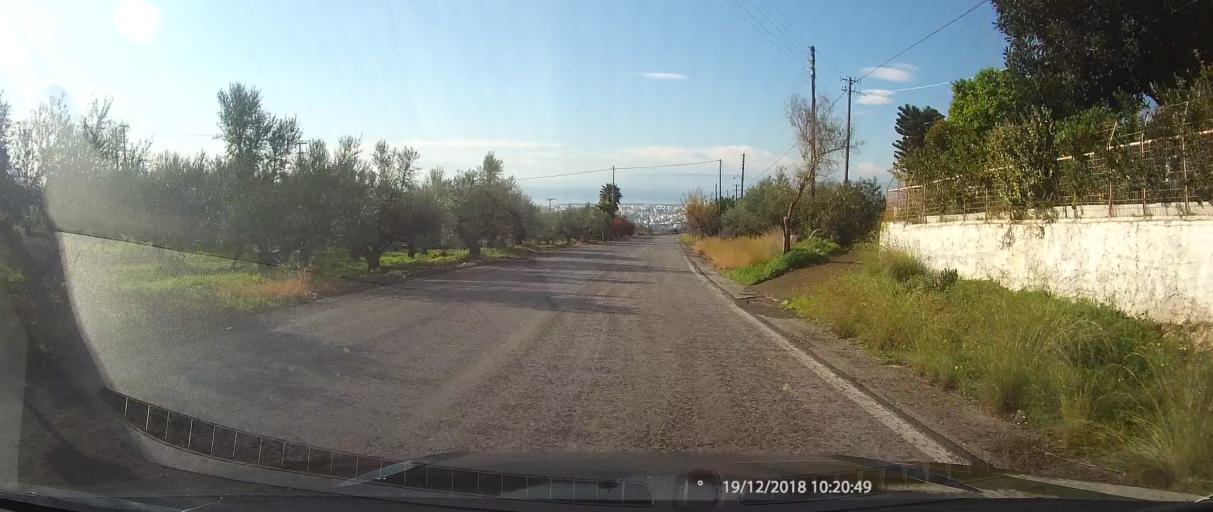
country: GR
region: Peloponnese
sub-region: Nomos Messinias
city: Kalamata
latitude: 37.0504
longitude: 22.1379
